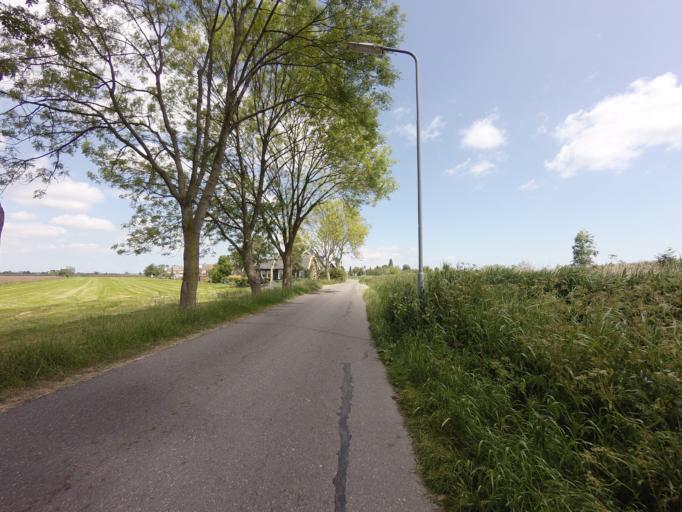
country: NL
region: North Holland
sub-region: Gemeente Beemster
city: Halfweg
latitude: 52.5868
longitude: 4.9747
